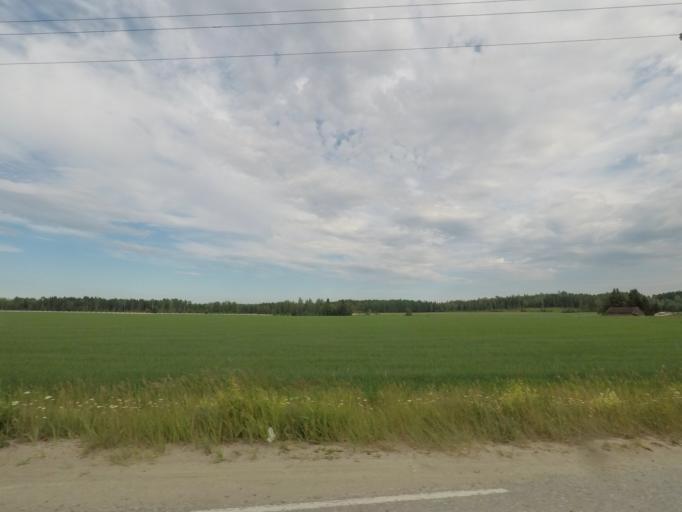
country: FI
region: Paijanne Tavastia
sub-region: Lahti
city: Lahti
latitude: 60.9259
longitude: 25.5793
